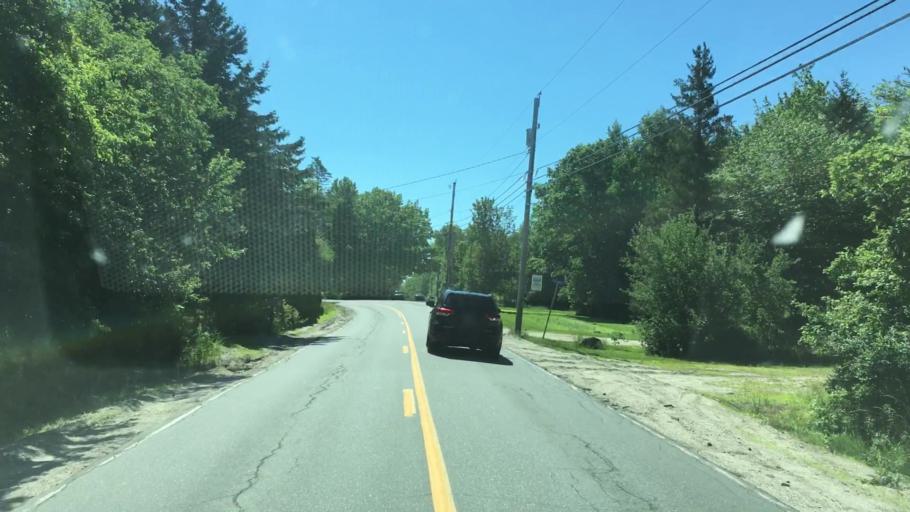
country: US
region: Maine
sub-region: Hancock County
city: Sedgwick
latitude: 44.4150
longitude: -68.6089
